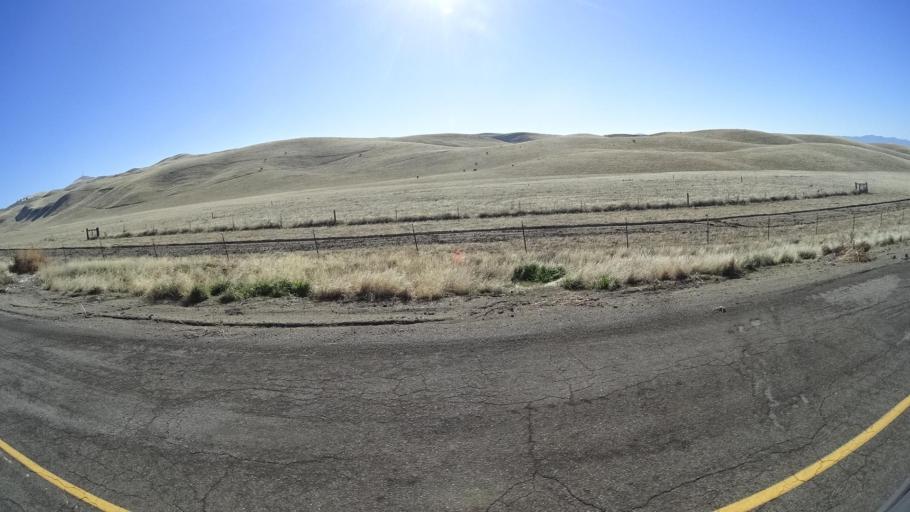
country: US
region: California
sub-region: Kern County
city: Maricopa
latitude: 34.9524
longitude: -119.4259
